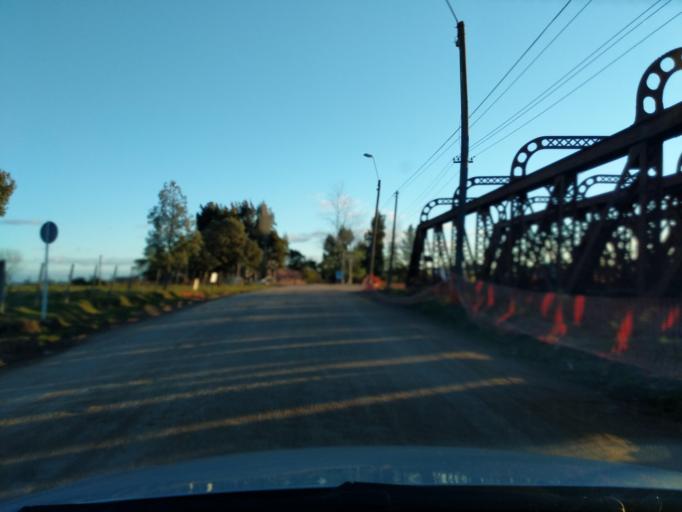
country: UY
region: Florida
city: Florida
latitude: -34.1041
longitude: -56.2421
